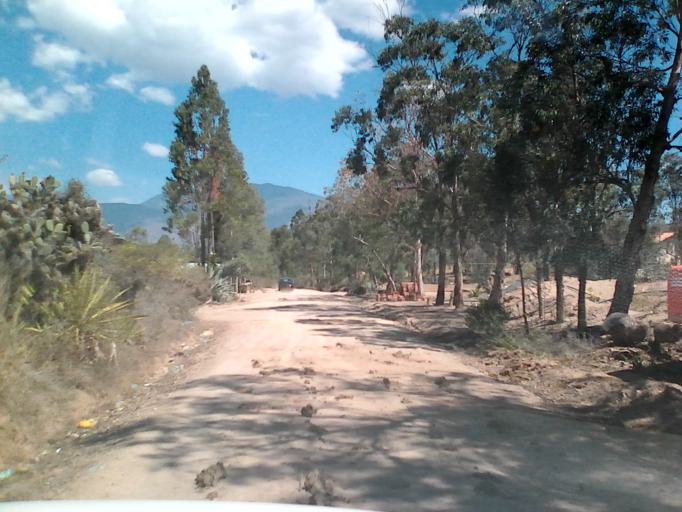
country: CO
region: Boyaca
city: Villa de Leiva
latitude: 5.6315
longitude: -73.5767
